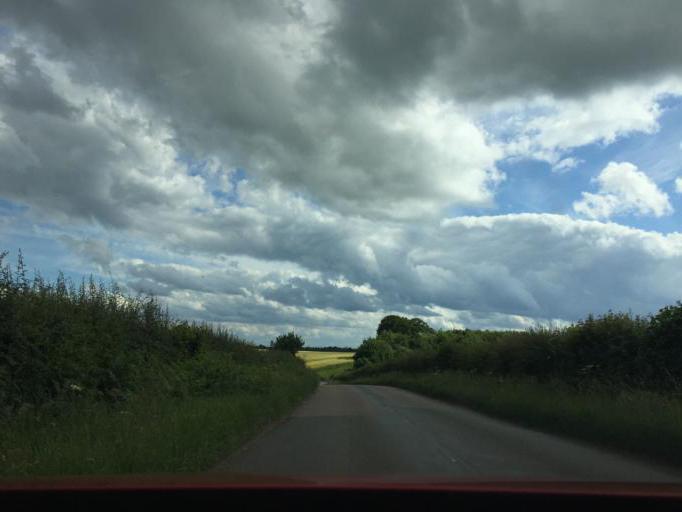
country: GB
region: England
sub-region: Hertfordshire
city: Harpenden
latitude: 51.8449
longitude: -0.3846
